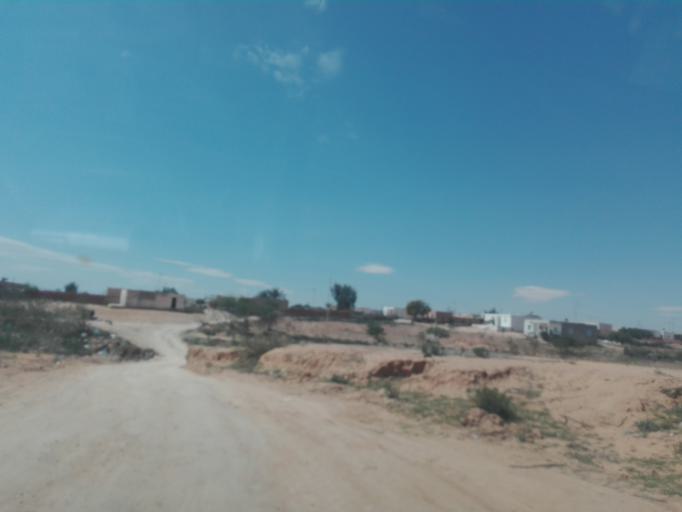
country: TN
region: Safaqis
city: Sfax
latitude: 34.6643
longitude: 10.5666
